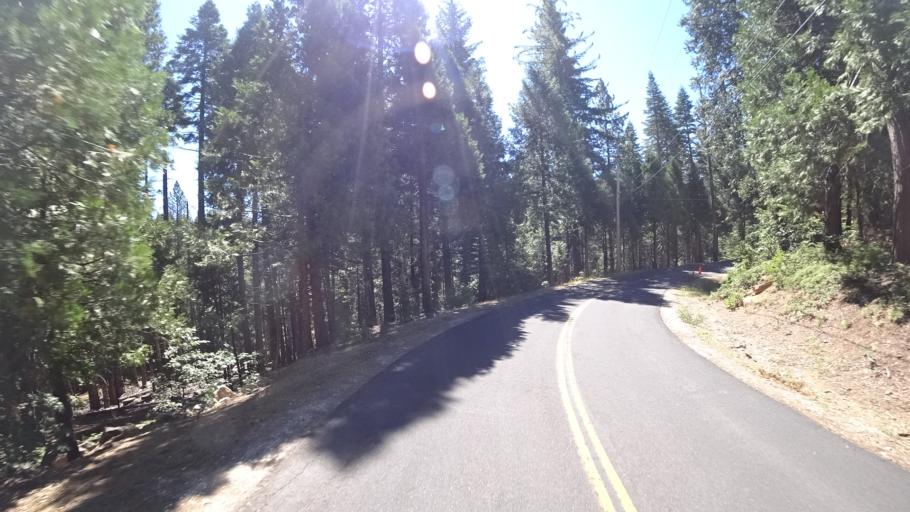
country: US
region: California
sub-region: Calaveras County
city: Arnold
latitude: 38.2988
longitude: -120.2764
